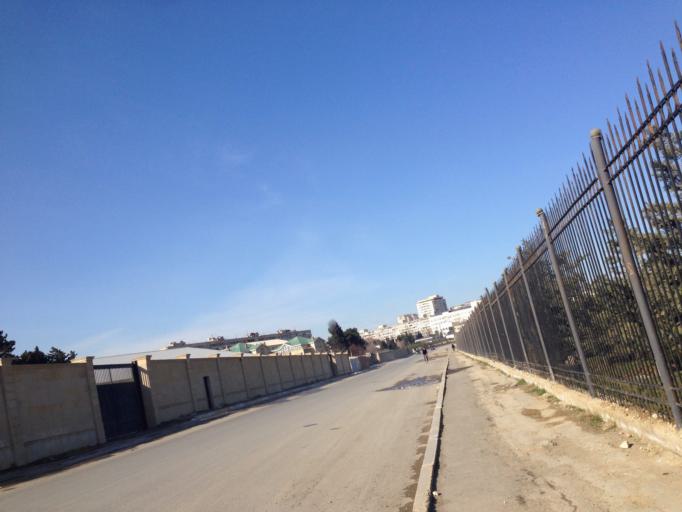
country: AZ
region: Baki
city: Baku
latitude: 40.4092
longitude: 49.8557
